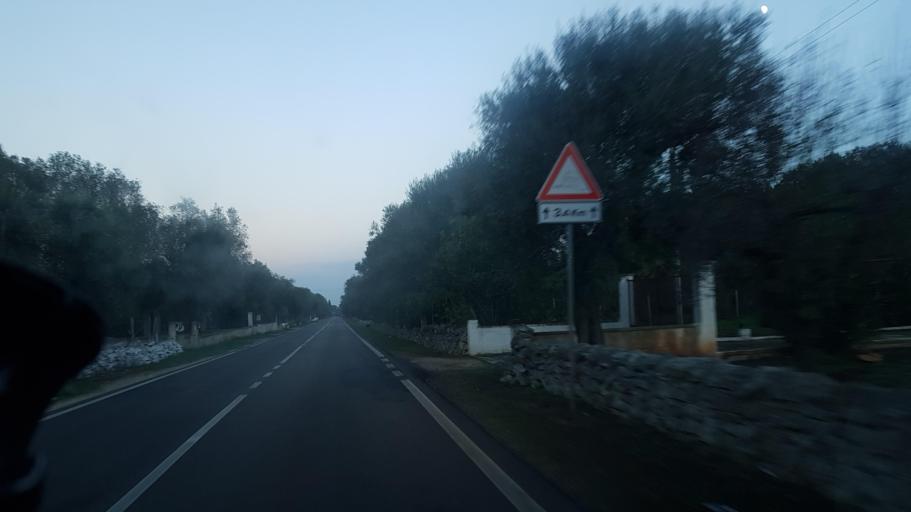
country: IT
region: Apulia
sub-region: Provincia di Brindisi
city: Latiano
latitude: 40.5686
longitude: 17.6778
